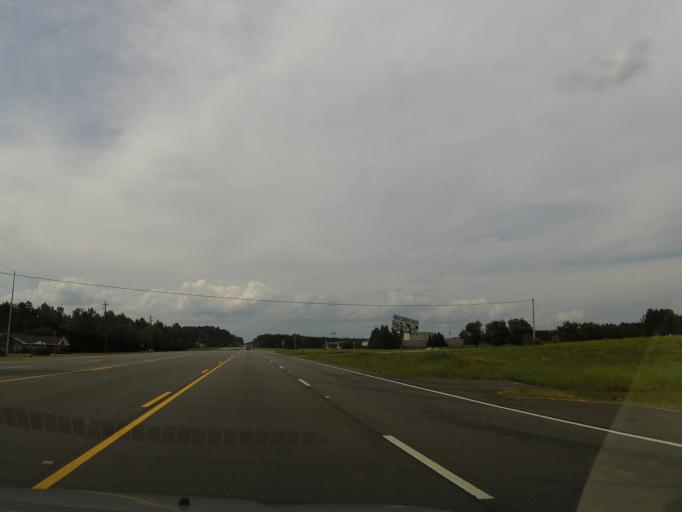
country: US
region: Georgia
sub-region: McDuffie County
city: Thomson
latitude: 33.5243
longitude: -82.5047
